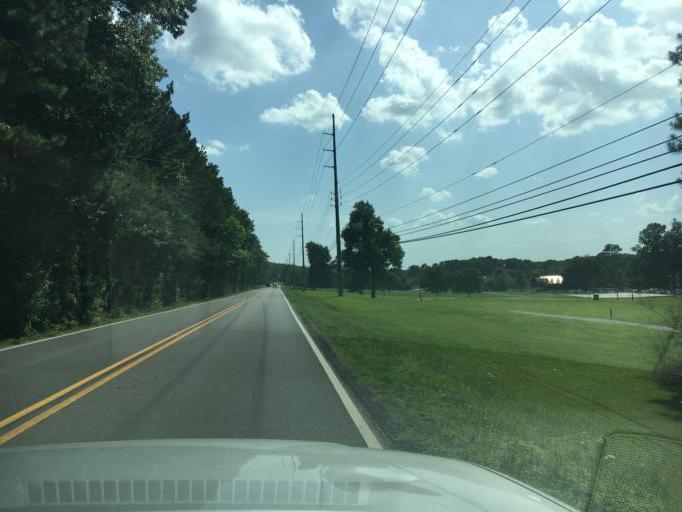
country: US
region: Alabama
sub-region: Shelby County
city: Meadowbrook
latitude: 33.3909
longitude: -86.7224
